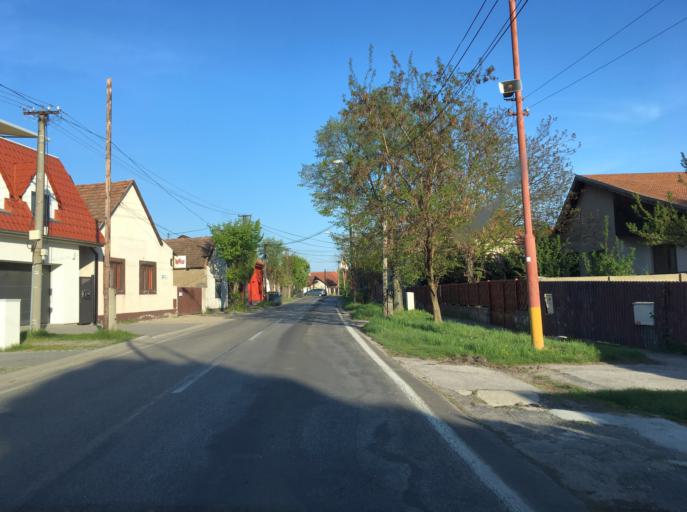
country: AT
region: Burgenland
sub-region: Politischer Bezirk Neusiedl am See
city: Deutsch Jahrndorf
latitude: 48.0573
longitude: 17.1413
